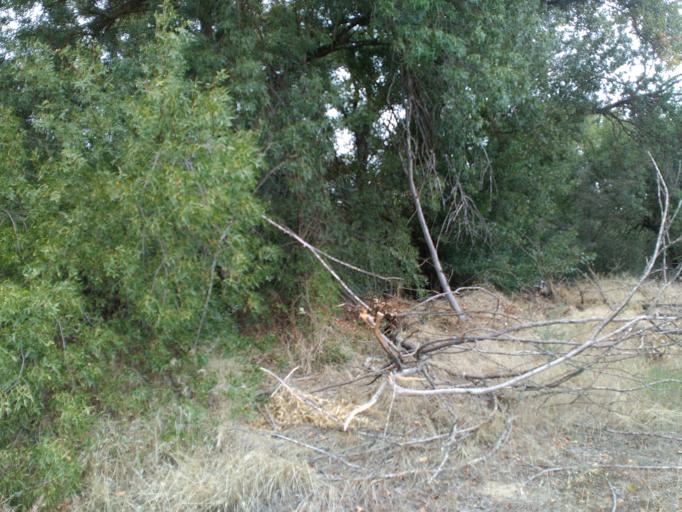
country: ES
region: Madrid
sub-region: Provincia de Madrid
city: Villanueva del Pardillo
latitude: 40.4961
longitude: -3.9354
